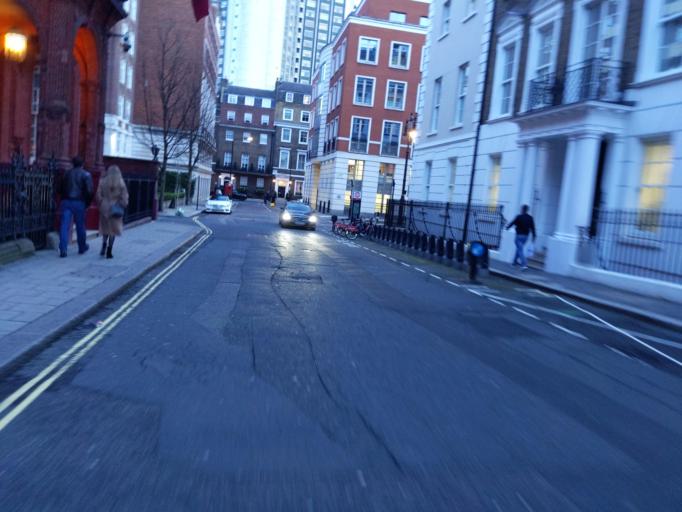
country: GB
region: England
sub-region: Greater London
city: London
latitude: 51.5071
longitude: -0.1507
